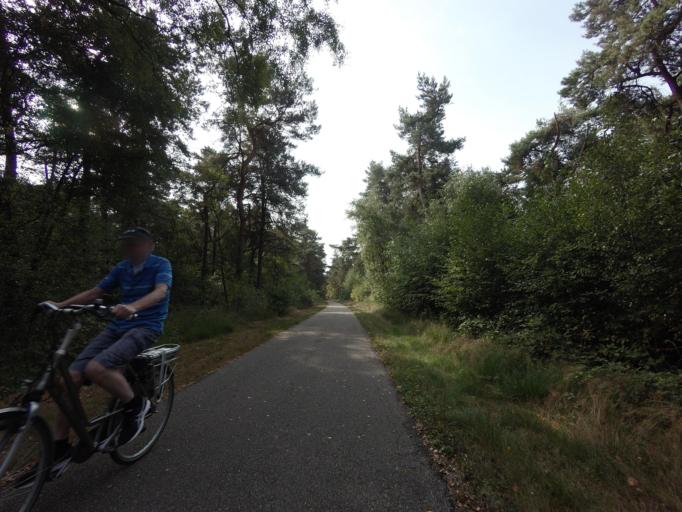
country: NL
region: North Brabant
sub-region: Gemeente Mill en Sint Hubert
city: Wilbertoord
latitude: 51.6152
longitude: 5.8163
